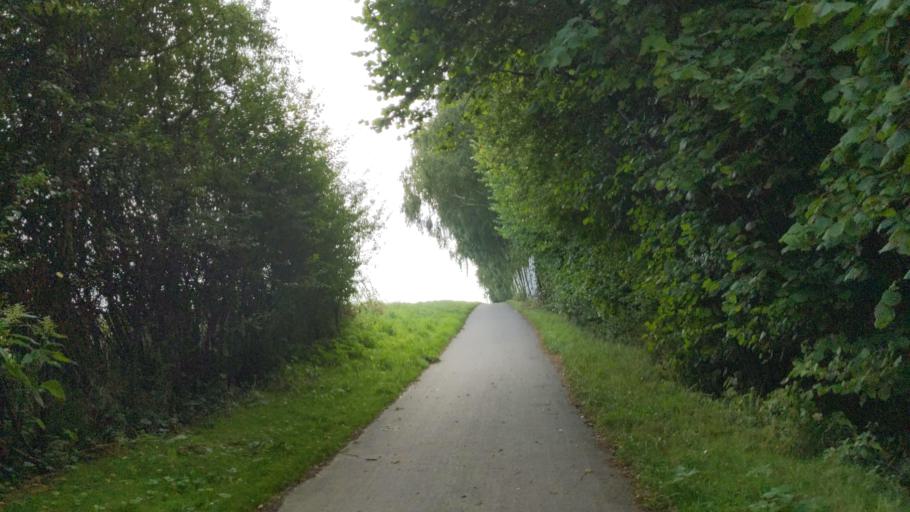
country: DE
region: Mecklenburg-Vorpommern
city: Dassow
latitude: 53.9775
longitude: 10.9650
